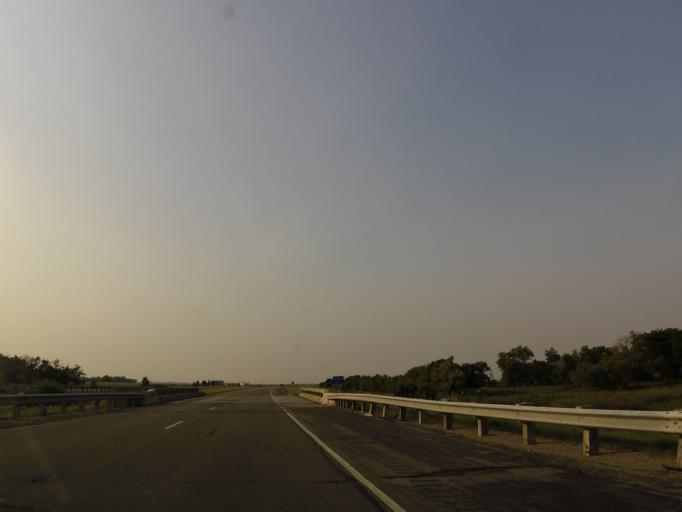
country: US
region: North Dakota
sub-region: Traill County
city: Hillsboro
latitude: 47.3257
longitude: -97.0461
